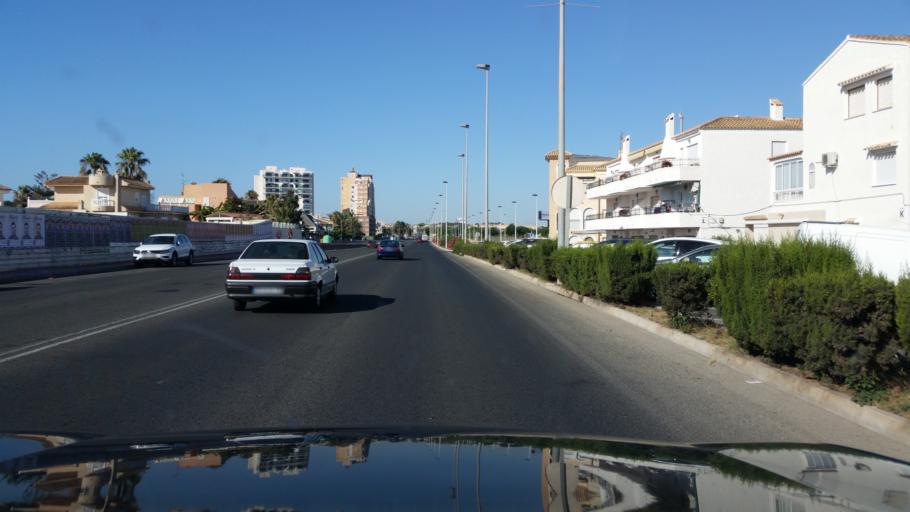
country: ES
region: Valencia
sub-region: Provincia de Alicante
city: Torrevieja
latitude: 37.9656
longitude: -0.7010
